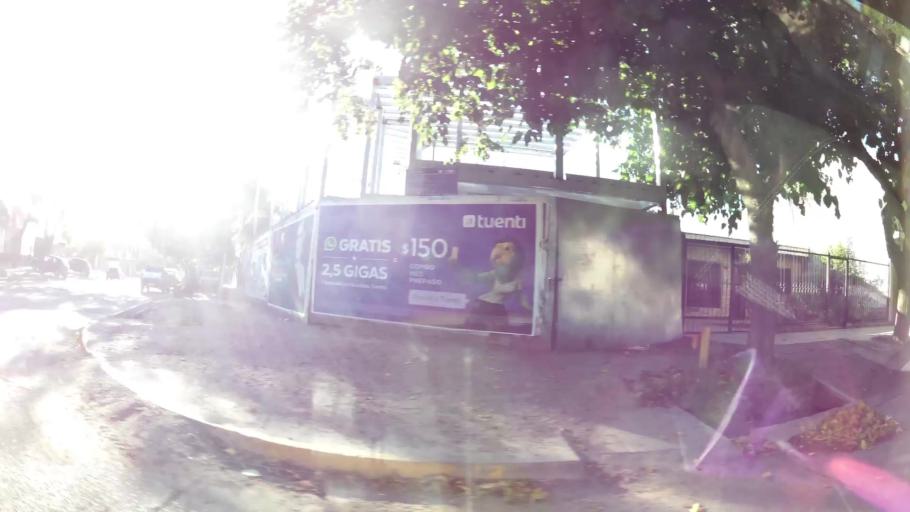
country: AR
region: Mendoza
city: Las Heras
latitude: -32.8714
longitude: -68.8196
